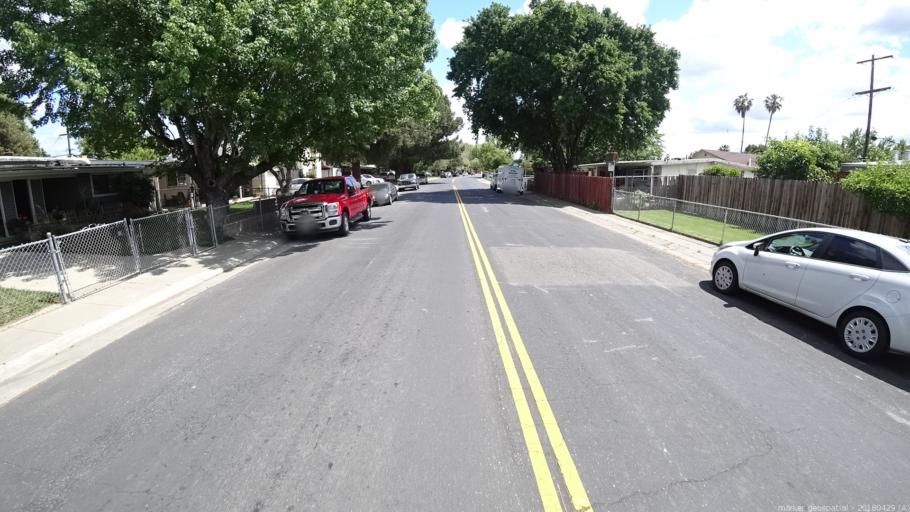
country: US
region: California
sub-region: Yolo County
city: West Sacramento
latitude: 38.5943
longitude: -121.5260
